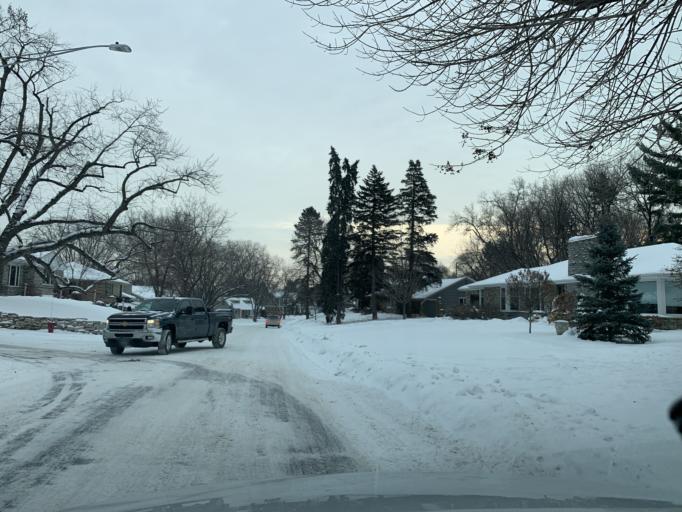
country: US
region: Minnesota
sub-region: Hennepin County
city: Edina
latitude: 44.9147
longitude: -93.3571
